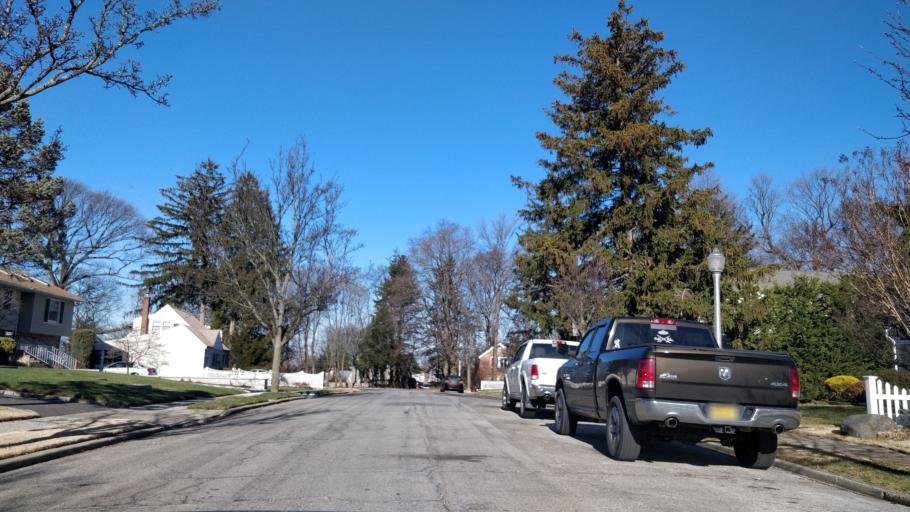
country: US
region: New York
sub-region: Nassau County
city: Glen Cove
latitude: 40.8744
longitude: -73.6249
